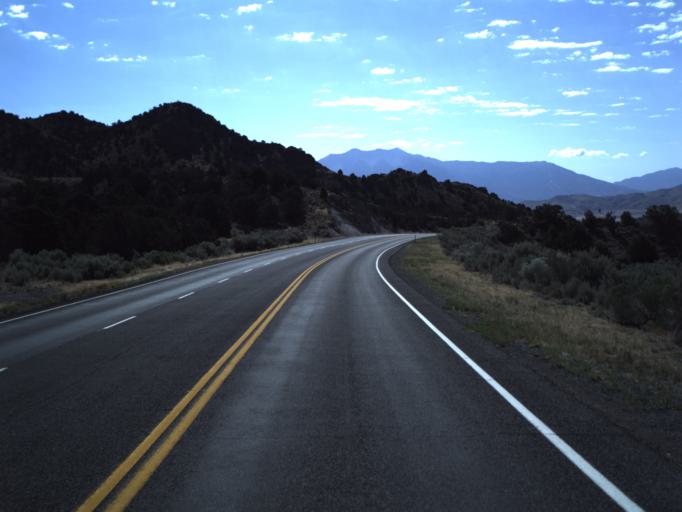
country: US
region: Utah
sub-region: Utah County
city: Genola
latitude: 39.9620
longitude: -112.0409
